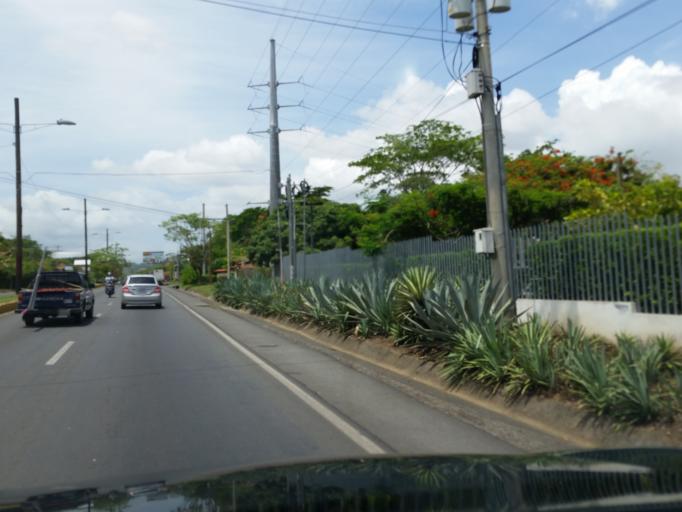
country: NI
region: Masaya
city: Ticuantepe
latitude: 12.0491
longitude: -86.1971
